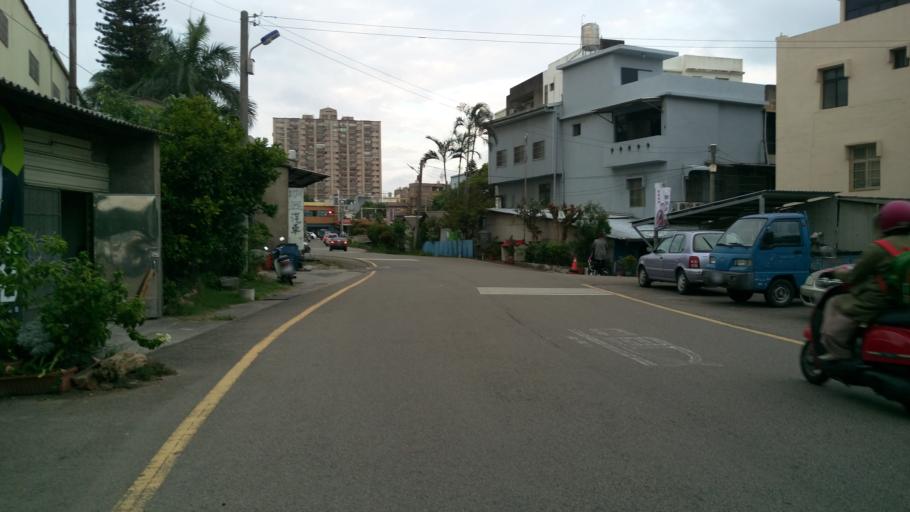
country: TW
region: Taiwan
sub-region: Hsinchu
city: Hsinchu
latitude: 24.8039
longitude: 120.9508
